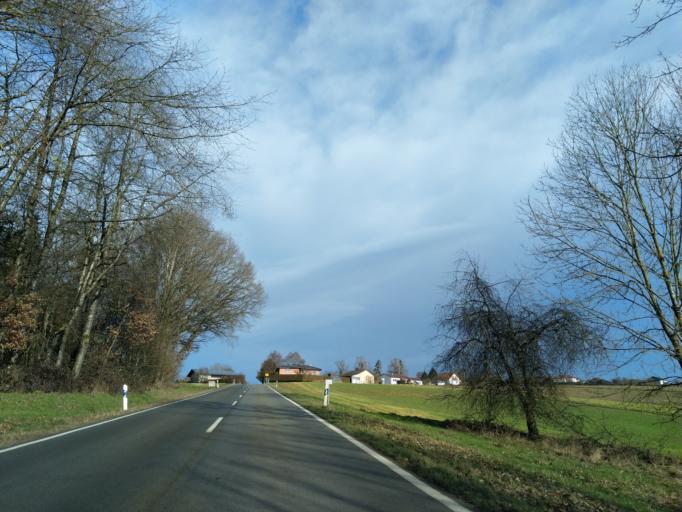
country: DE
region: Bavaria
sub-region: Lower Bavaria
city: Aldersbach
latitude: 48.6286
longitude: 13.0217
